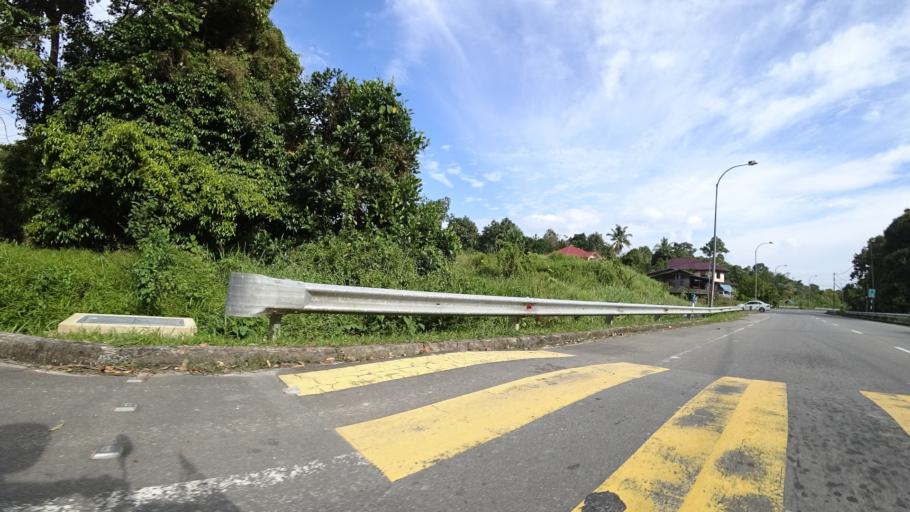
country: BN
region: Brunei and Muara
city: Bandar Seri Begawan
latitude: 4.8809
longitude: 114.8021
